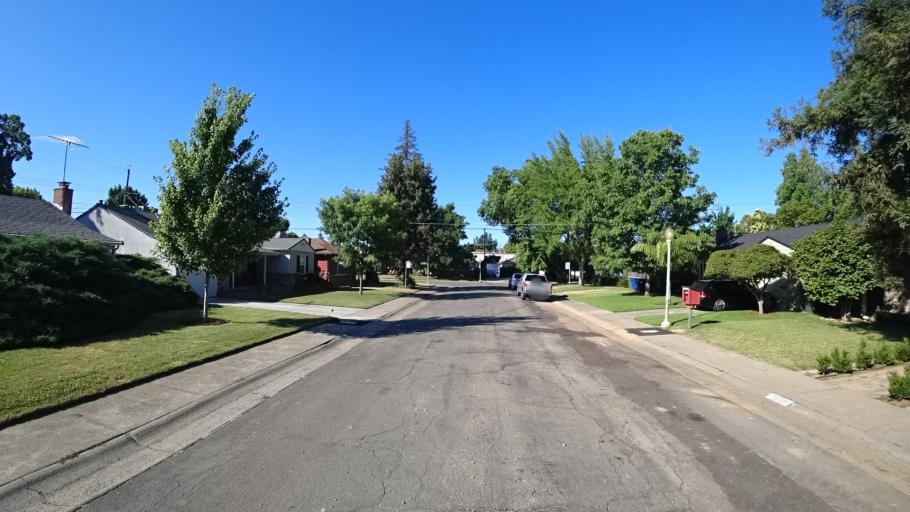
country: US
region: California
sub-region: Sacramento County
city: Florin
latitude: 38.5575
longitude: -121.4312
